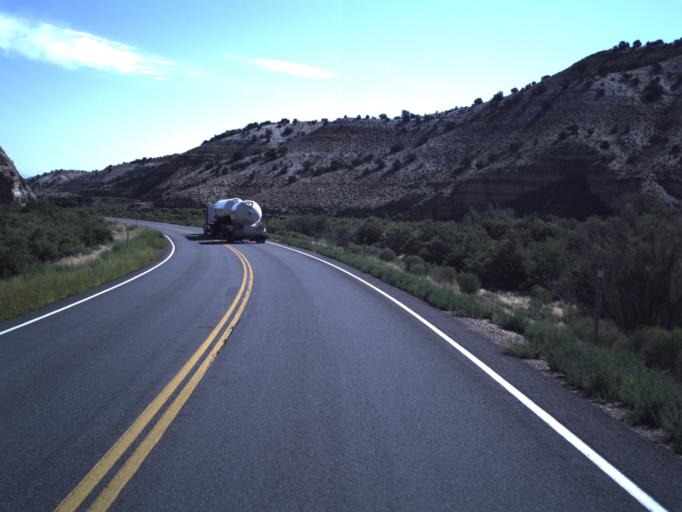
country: US
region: Utah
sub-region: Duchesne County
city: Duchesne
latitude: 40.1094
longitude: -110.4589
